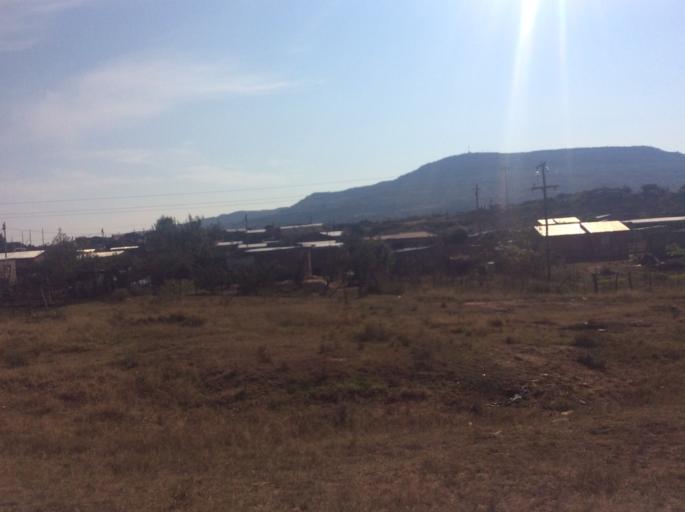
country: LS
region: Mafeteng
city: Mafeteng
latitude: -29.7217
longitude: 27.0175
